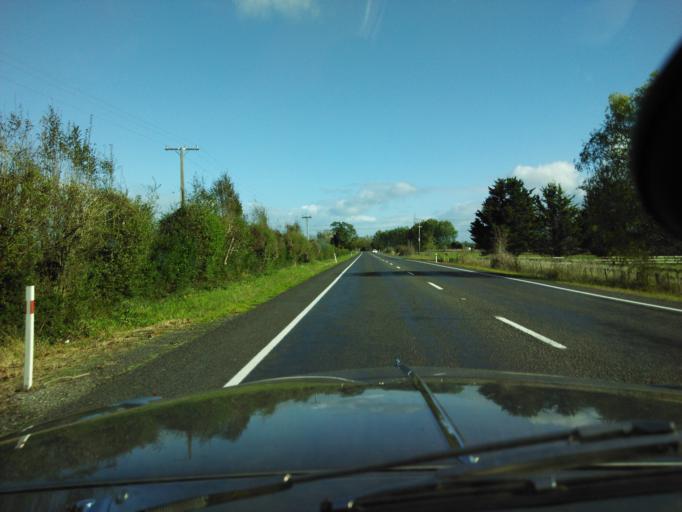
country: NZ
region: Waikato
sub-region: Hauraki District
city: Paeroa
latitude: -37.5603
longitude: 175.6874
